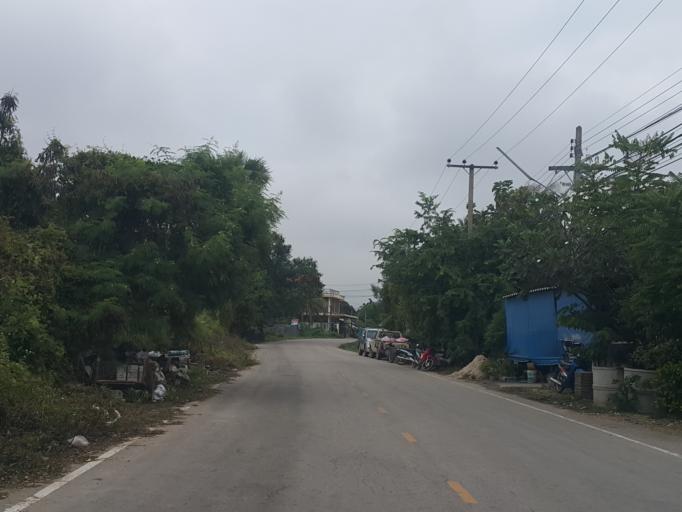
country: TH
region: Lampang
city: Lampang
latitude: 18.3170
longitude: 99.4921
